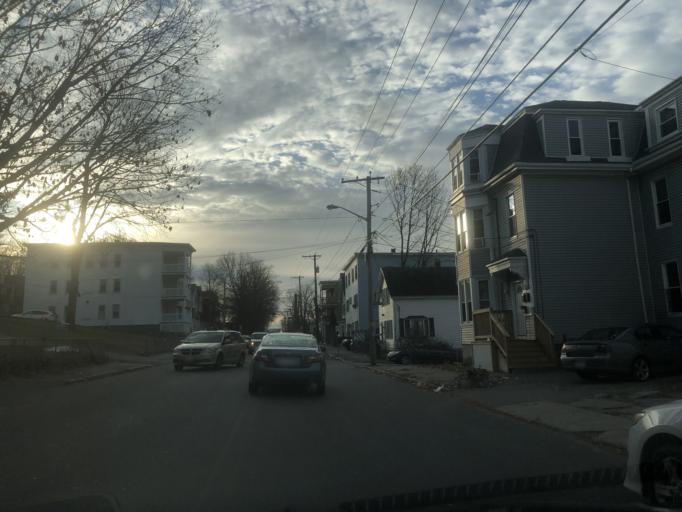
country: US
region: Massachusetts
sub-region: Essex County
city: Lawrence
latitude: 42.7139
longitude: -71.1523
